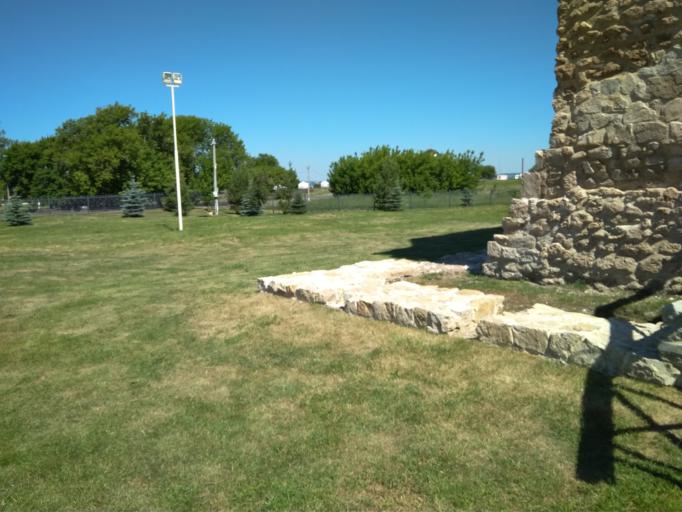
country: RU
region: Tatarstan
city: Bolgar
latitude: 54.9820
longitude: 49.0540
